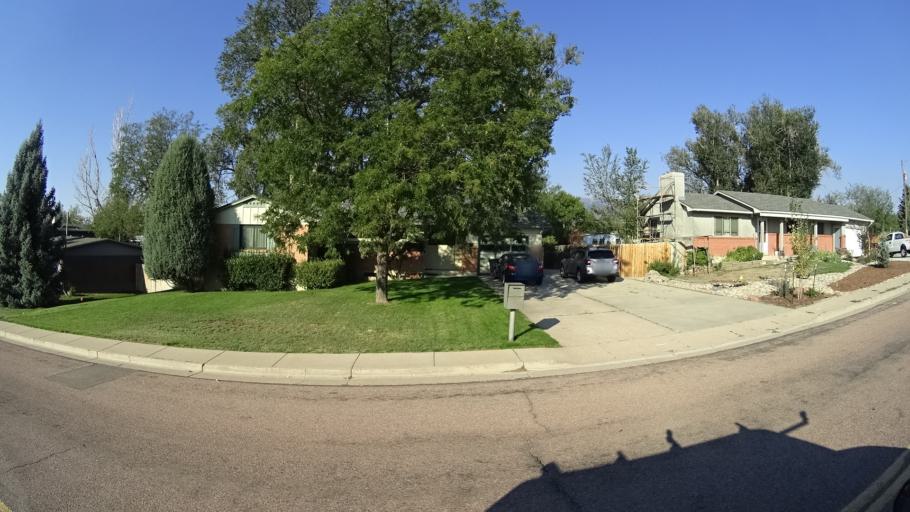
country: US
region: Colorado
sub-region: El Paso County
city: Stratmoor
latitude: 38.7766
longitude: -104.7911
